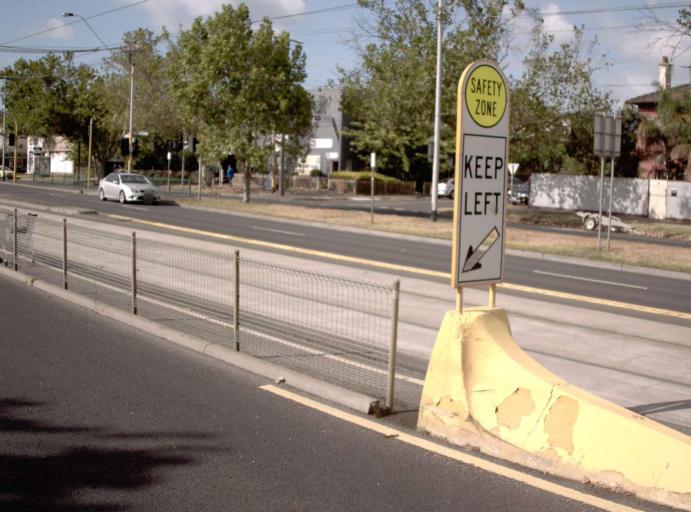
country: AU
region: Victoria
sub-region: Port Phillip
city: Balaclava
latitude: -37.8714
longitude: 144.9893
